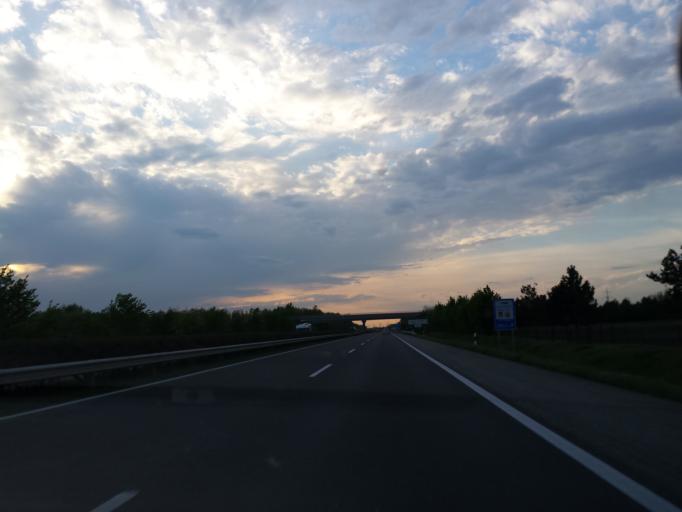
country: HU
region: Gyor-Moson-Sopron
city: Mosonszentmiklos
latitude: 47.7419
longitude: 17.4292
